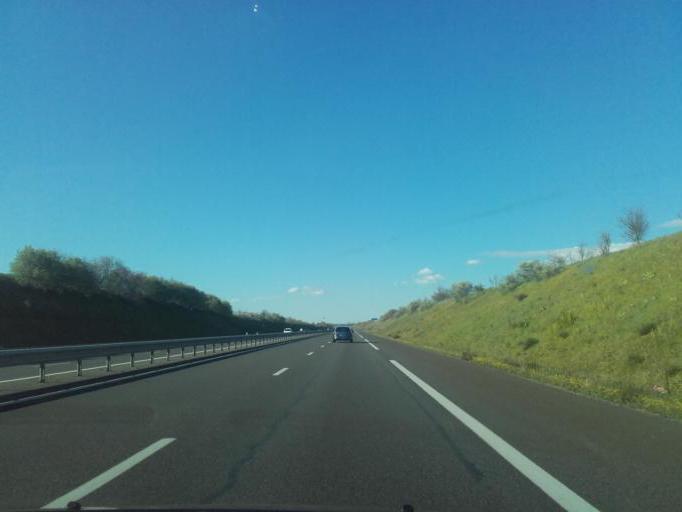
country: FR
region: Rhone-Alpes
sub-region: Departement de l'Isere
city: Janneyrias
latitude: 45.7330
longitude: 5.0958
